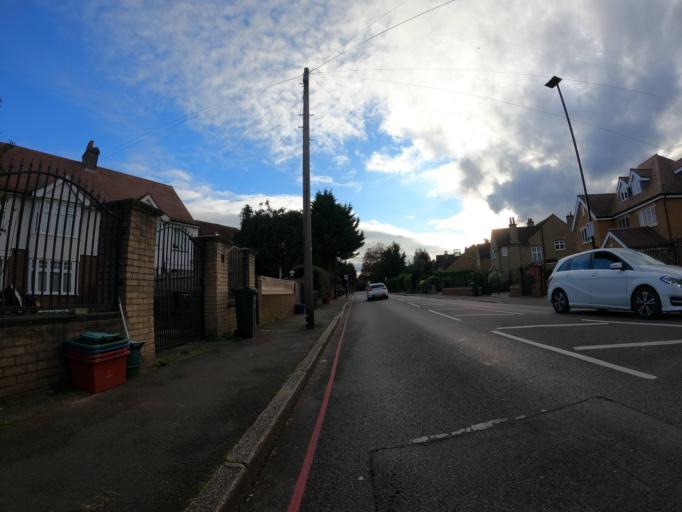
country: GB
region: England
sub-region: Greater London
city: Isleworth
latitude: 51.4877
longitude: -0.3410
